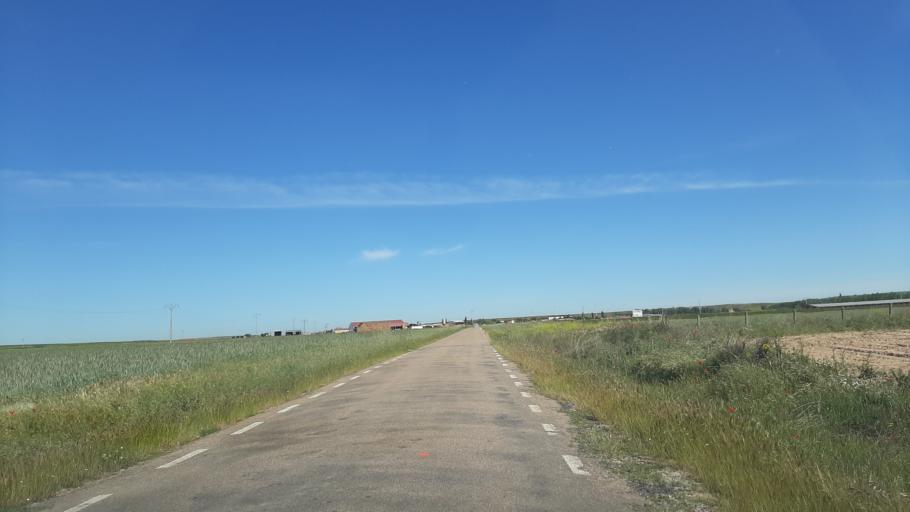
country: ES
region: Castille and Leon
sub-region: Provincia de Salamanca
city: Pedrosillo de Alba
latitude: 40.8142
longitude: -5.3872
